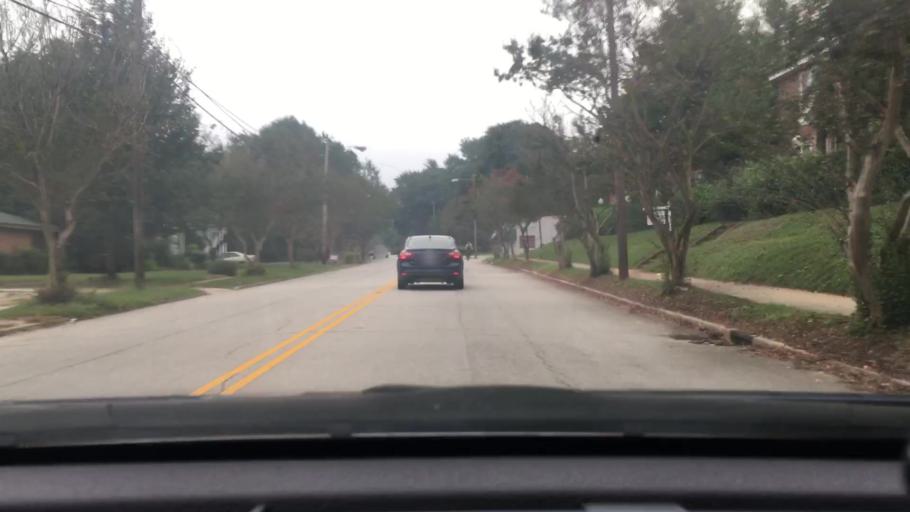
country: US
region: South Carolina
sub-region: Richland County
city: Columbia
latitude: 34.0275
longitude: -81.0537
